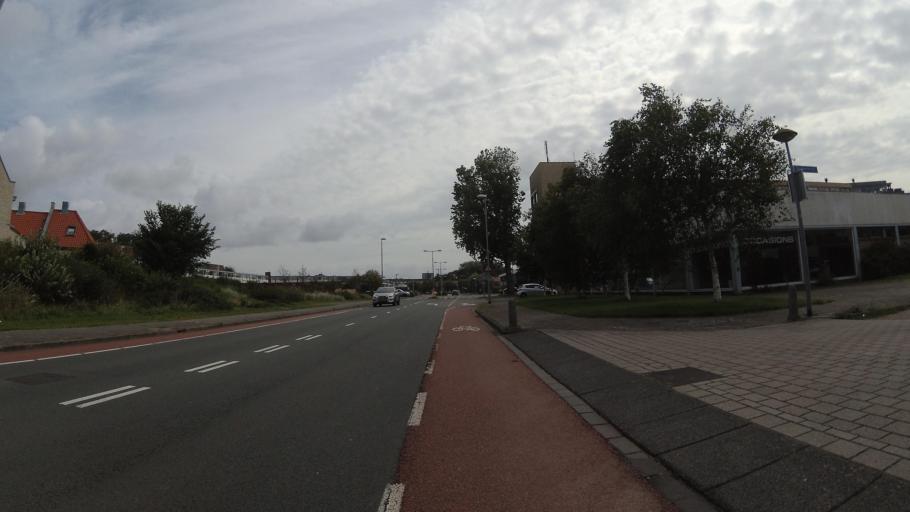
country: NL
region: North Holland
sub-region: Gemeente Den Helder
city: Den Helder
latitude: 52.9390
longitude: 4.7380
